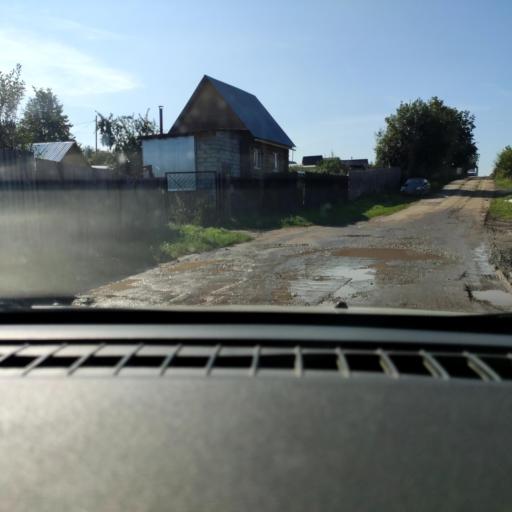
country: RU
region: Perm
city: Novyye Lyady
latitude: 58.0574
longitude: 56.5834
